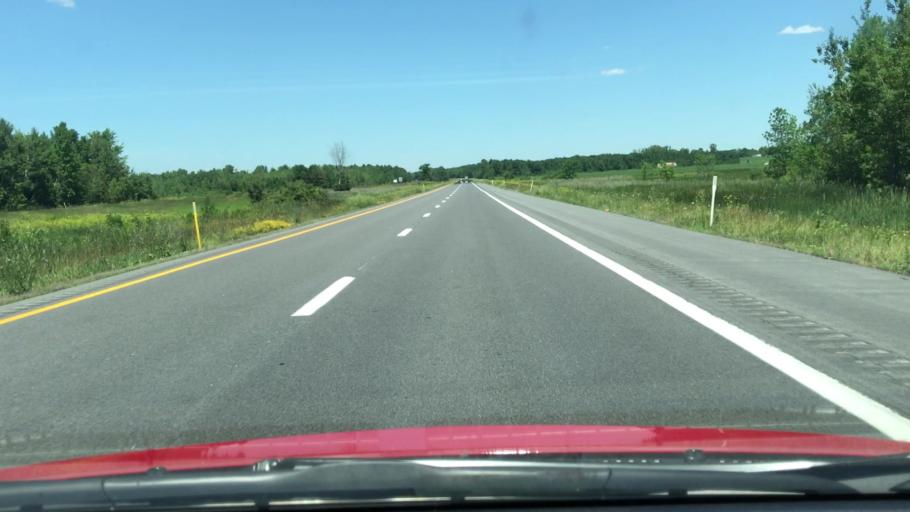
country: US
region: New York
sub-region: Clinton County
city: Cumberland Head
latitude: 44.8307
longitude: -73.4464
